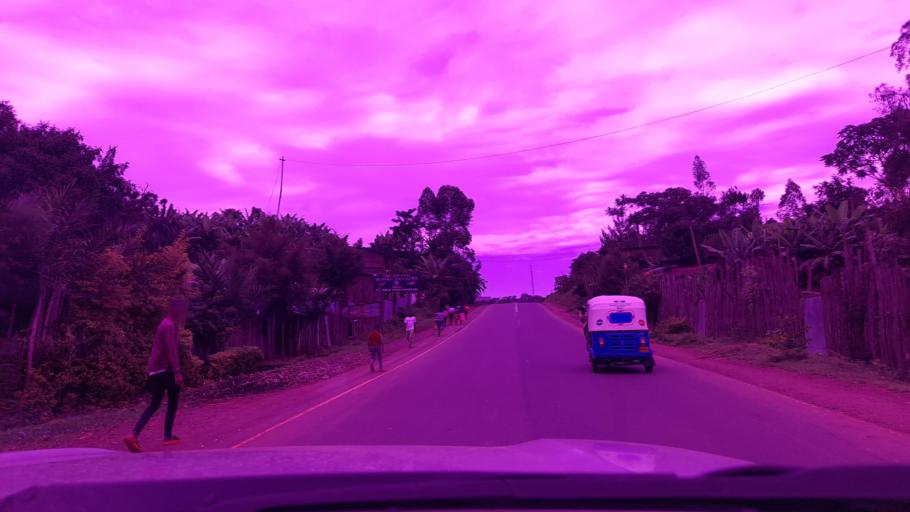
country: ET
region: Southern Nations, Nationalities, and People's Region
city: Mizan Teferi
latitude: 7.0023
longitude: 35.5993
